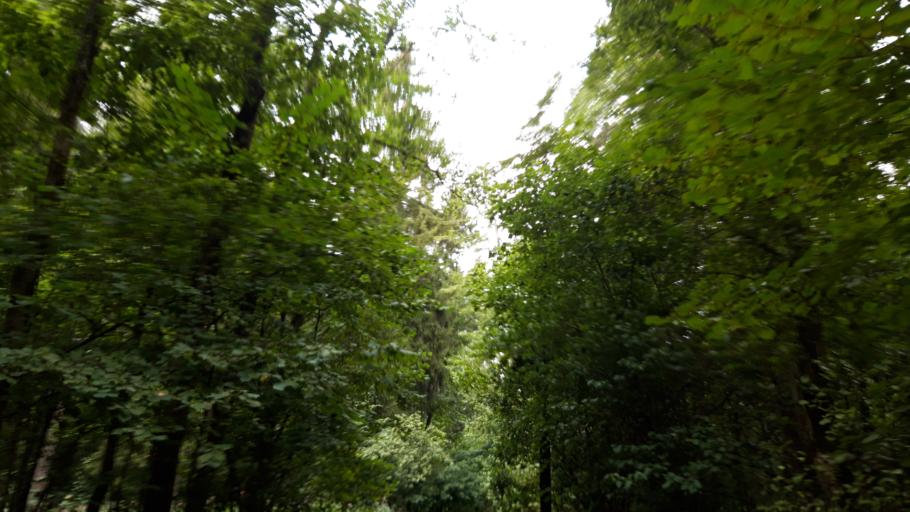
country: RU
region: Moscow
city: Zelenograd
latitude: 55.9907
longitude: 37.1980
